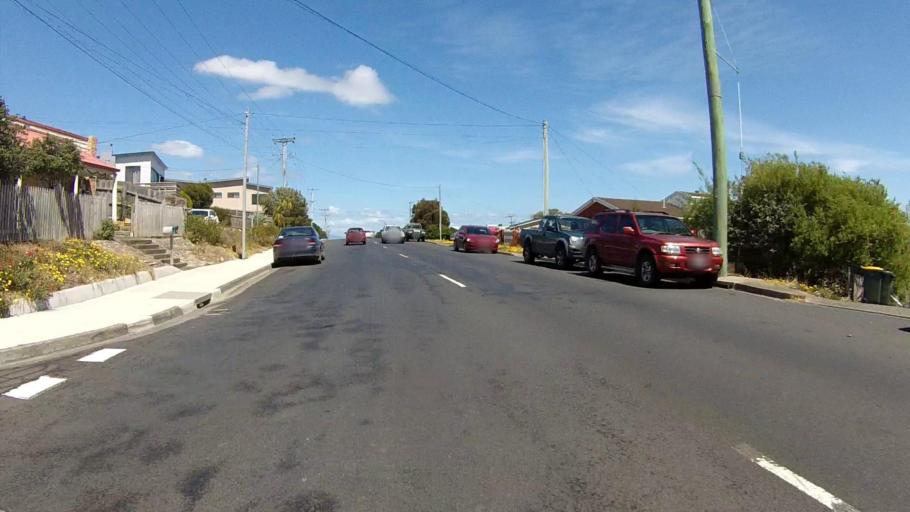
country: AU
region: Tasmania
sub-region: Sorell
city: Sorell
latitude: -42.7997
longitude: 147.5286
